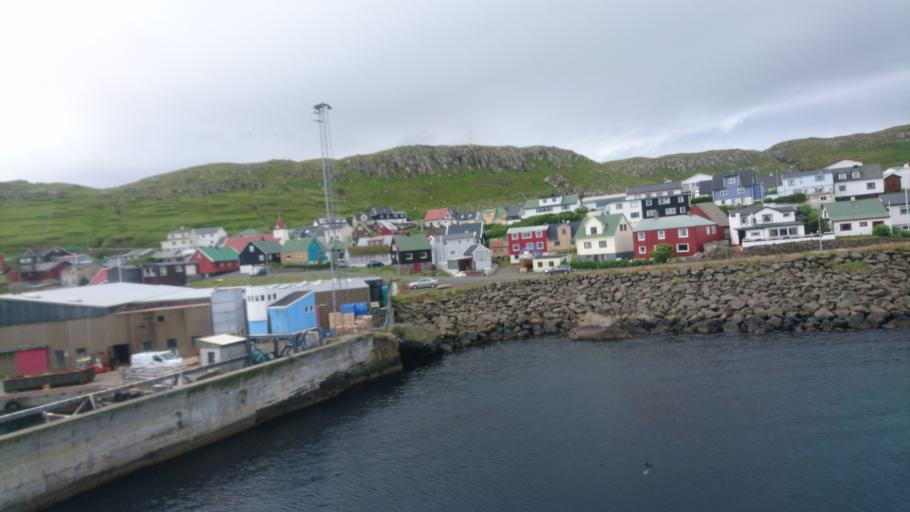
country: FO
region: Sandoy
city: Sandur
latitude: 61.9040
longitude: -6.8803
